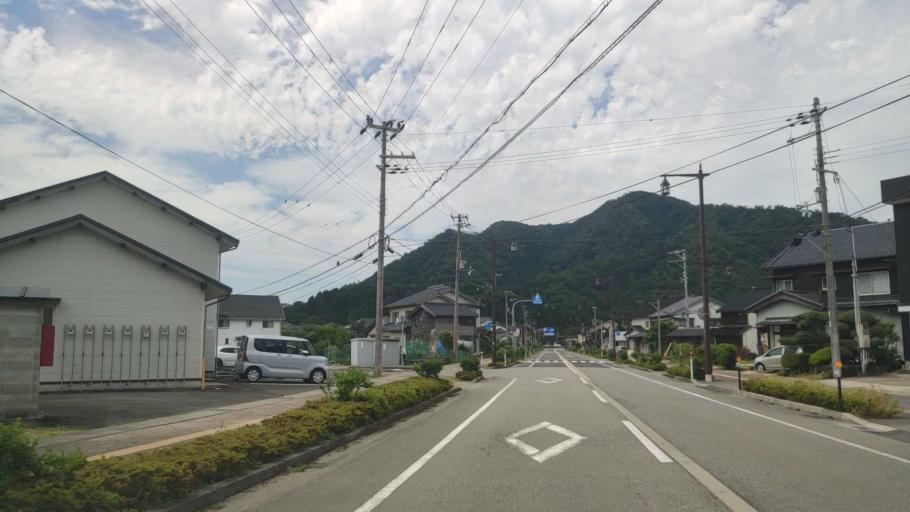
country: JP
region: Hyogo
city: Toyooka
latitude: 35.6527
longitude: 134.7594
